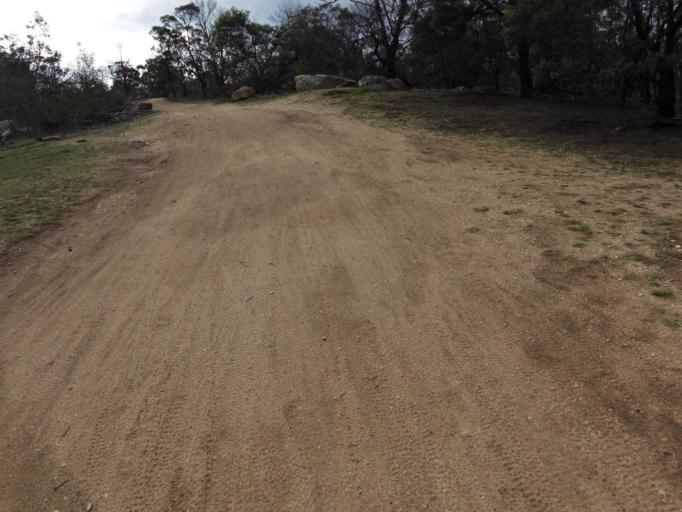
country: AU
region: Victoria
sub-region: Wyndham
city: Little River
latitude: -37.9358
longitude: 144.4358
